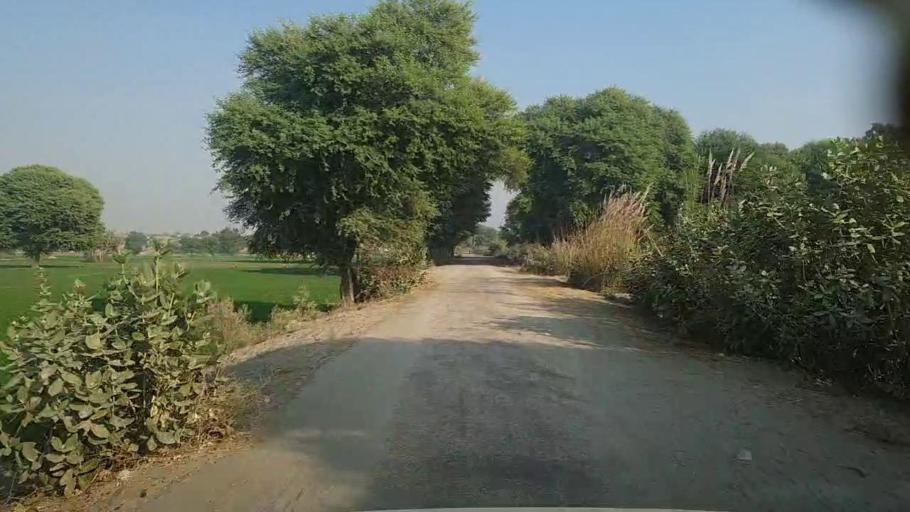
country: PK
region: Sindh
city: Karaundi
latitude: 26.7660
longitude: 68.4801
